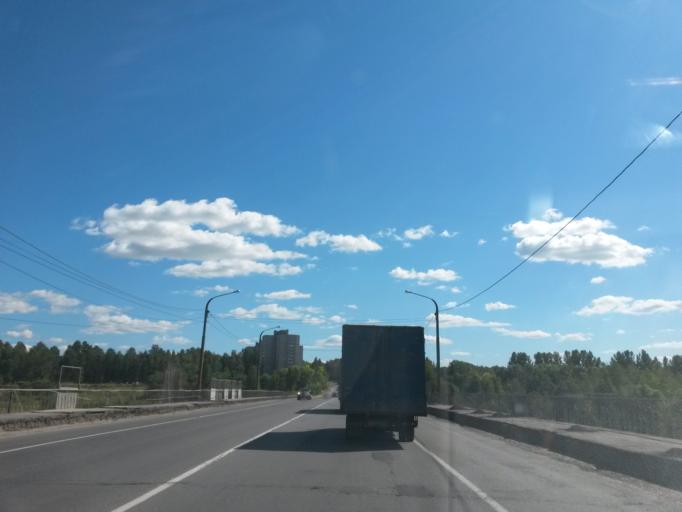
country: RU
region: Jaroslavl
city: Yaroslavl
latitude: 57.5888
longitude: 39.8187
